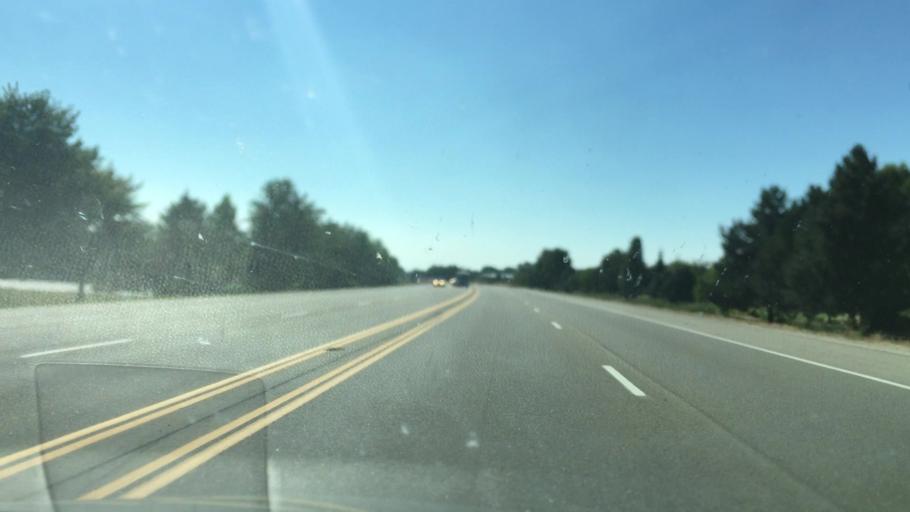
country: US
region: Idaho
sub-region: Ada County
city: Eagle
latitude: 43.6892
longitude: -116.3397
